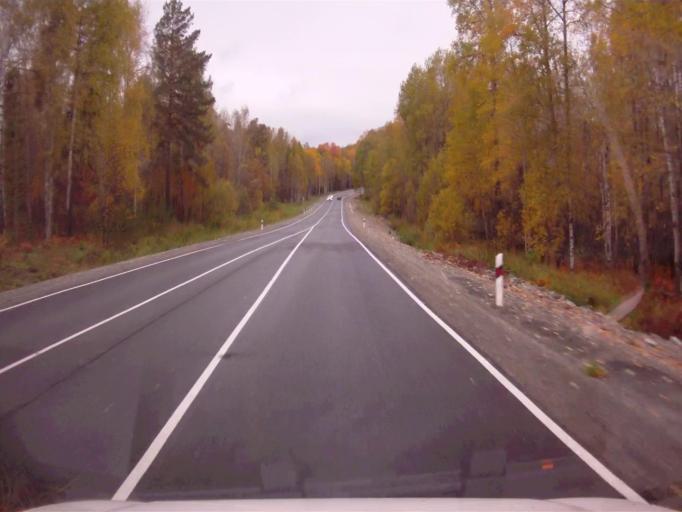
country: RU
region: Chelyabinsk
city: Nyazepetrovsk
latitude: 56.0667
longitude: 59.6988
